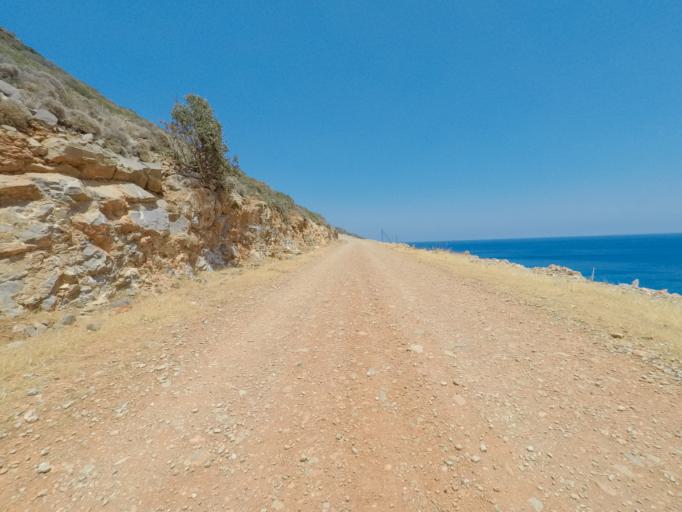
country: GR
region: Crete
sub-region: Nomos Lasithiou
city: Elounda
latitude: 35.3102
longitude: 25.7427
